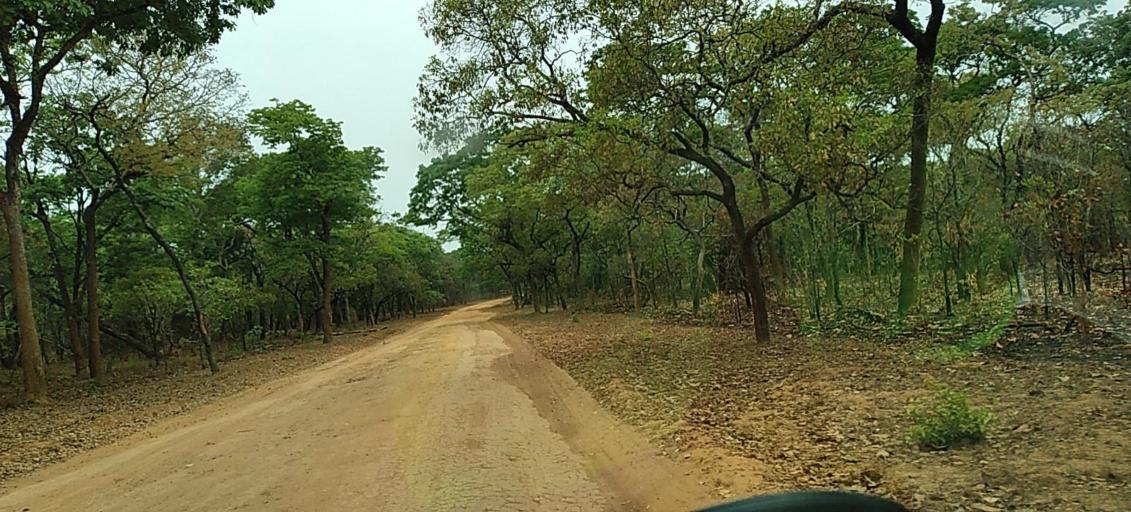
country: ZM
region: North-Western
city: Solwezi
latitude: -12.9161
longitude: 26.5585
